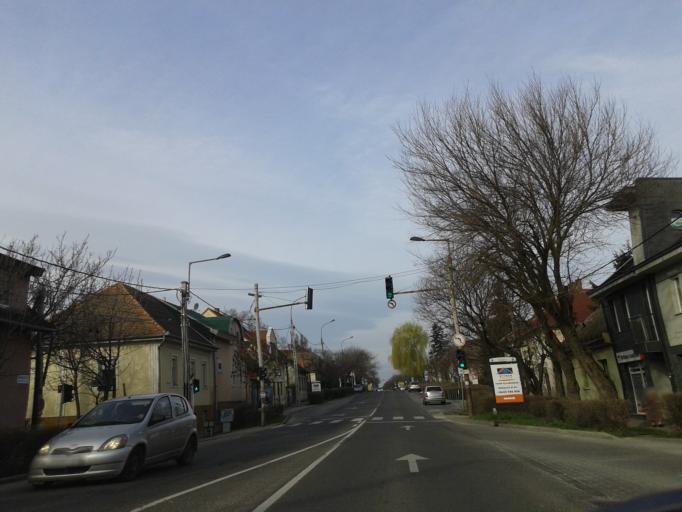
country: HU
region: Pest
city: Budaors
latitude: 47.4624
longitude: 18.9741
